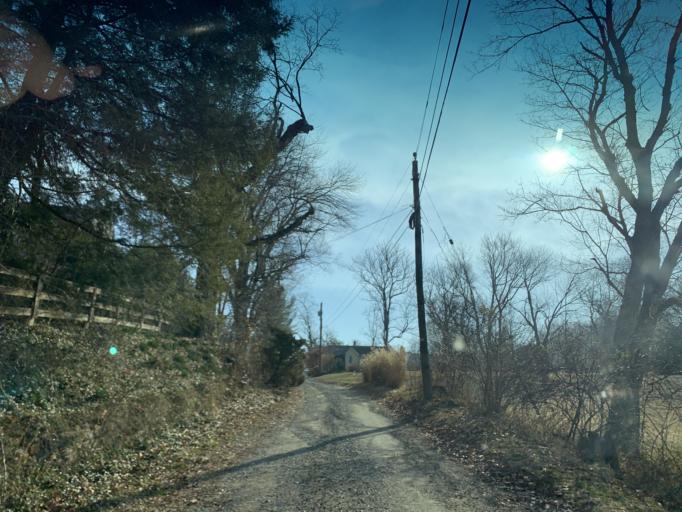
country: US
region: Maryland
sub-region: Harford County
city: Aberdeen
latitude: 39.6105
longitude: -76.2168
